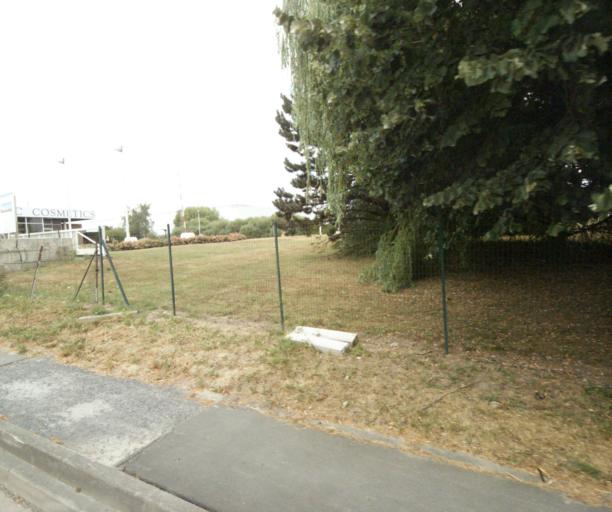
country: FR
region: Nord-Pas-de-Calais
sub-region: Departement du Nord
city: Neuville-en-Ferrain
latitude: 50.7588
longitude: 3.1614
